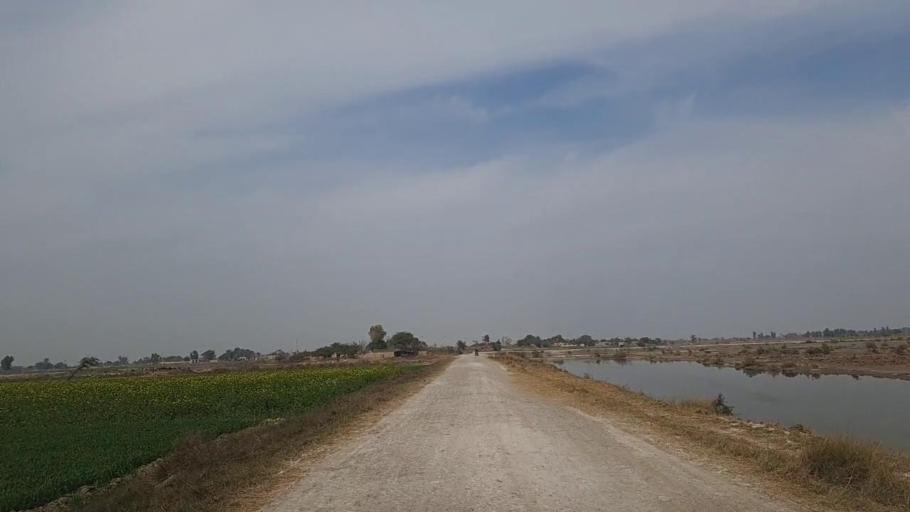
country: PK
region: Sindh
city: Daur
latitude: 26.4758
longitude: 68.4024
